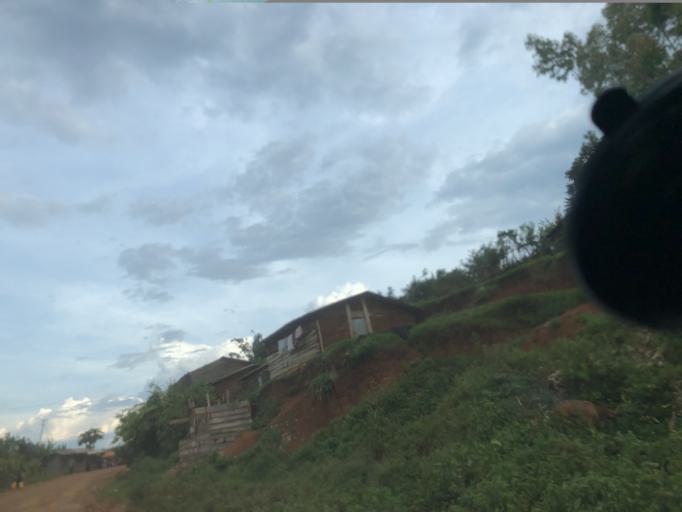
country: RW
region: Western Province
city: Cyangugu
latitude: -2.1923
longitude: 28.8486
